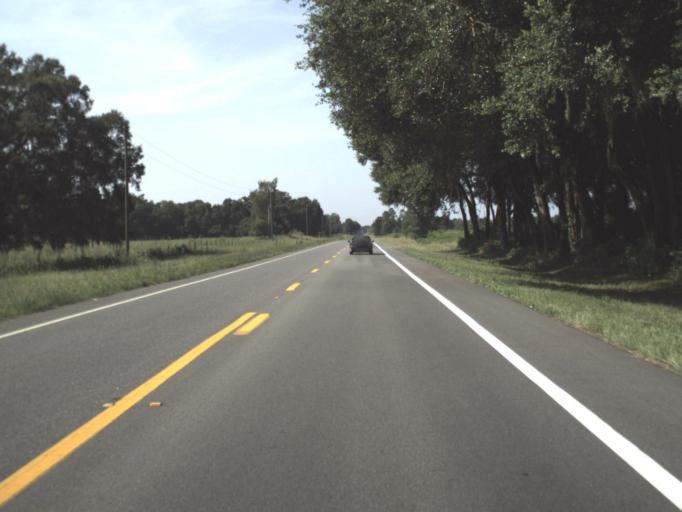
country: US
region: Florida
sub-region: Alachua County
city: High Springs
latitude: 29.9479
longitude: -82.7134
